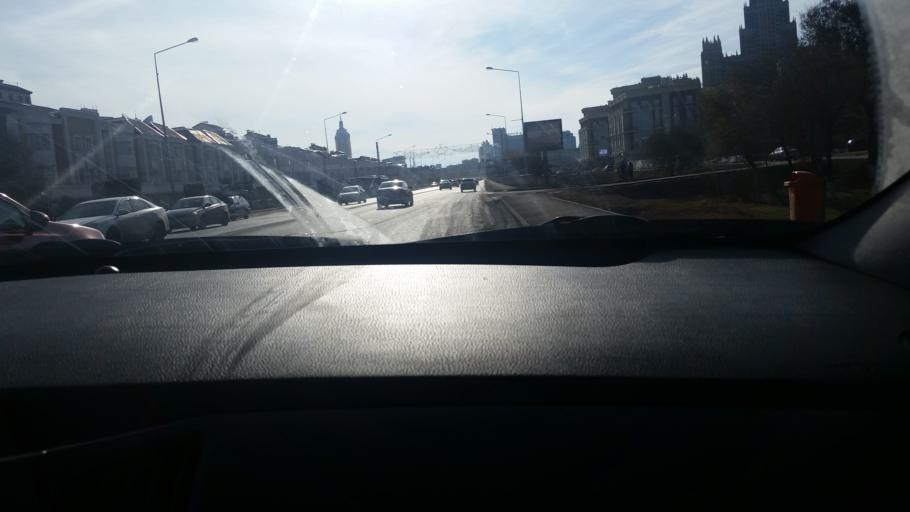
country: KZ
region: Astana Qalasy
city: Astana
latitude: 51.1443
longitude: 71.4205
